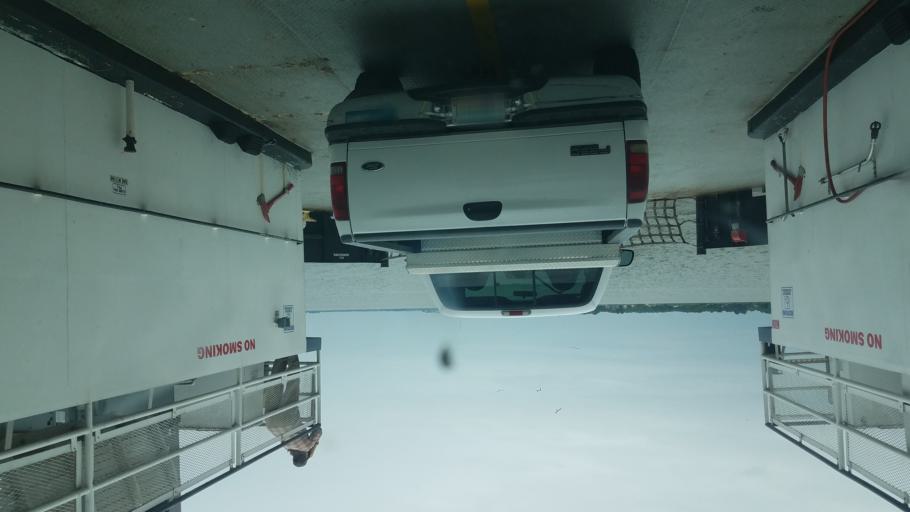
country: US
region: North Carolina
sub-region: Currituck County
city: Currituck
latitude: 36.4757
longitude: -75.9413
